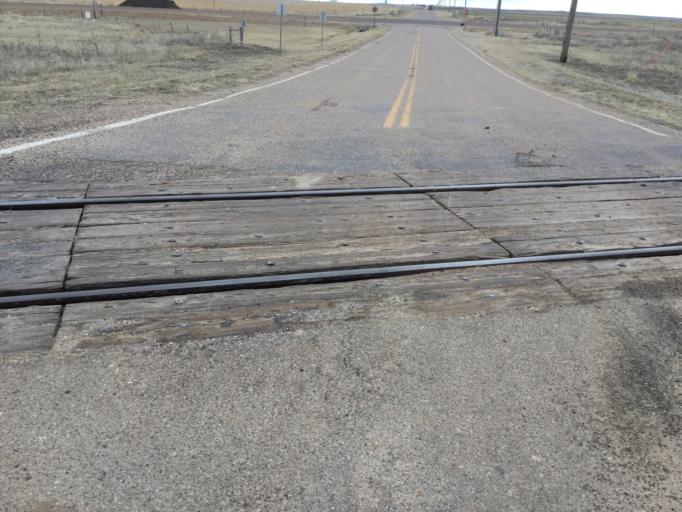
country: US
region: Kansas
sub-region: Morton County
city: Elkhart
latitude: 37.0751
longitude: -101.7728
